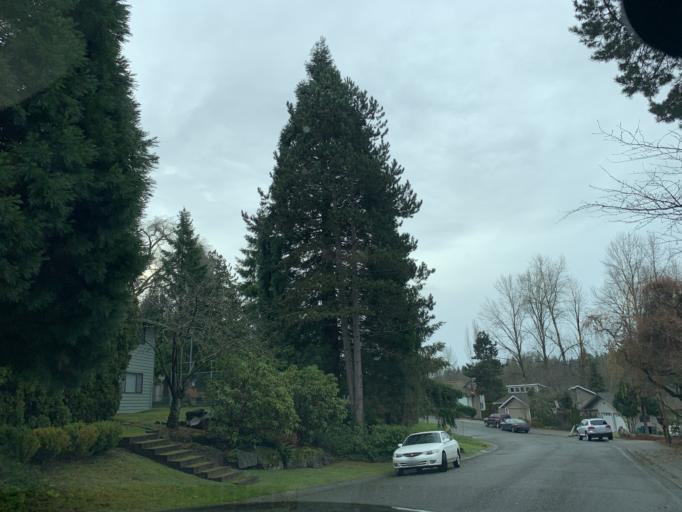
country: US
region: Washington
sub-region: King County
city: Woodinville
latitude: 47.7450
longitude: -122.1771
